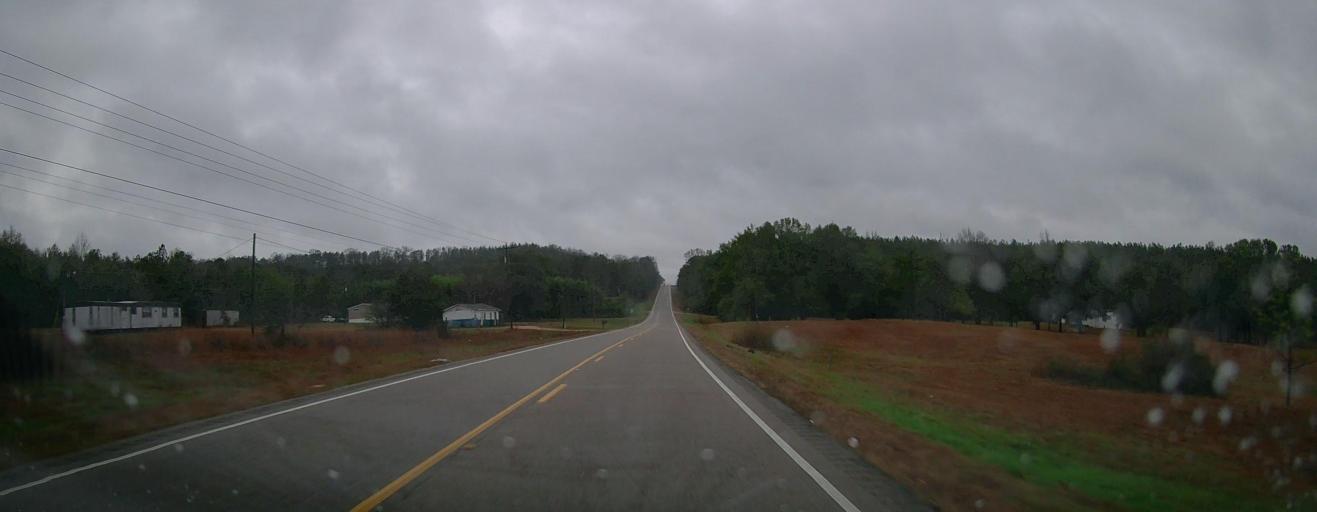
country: US
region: Alabama
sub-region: Autauga County
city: Pine Level
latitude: 32.5238
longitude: -86.6262
